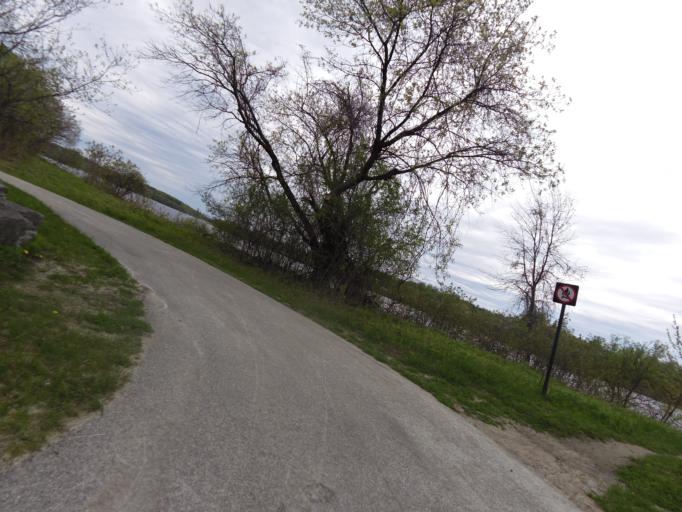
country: CA
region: Quebec
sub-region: Outaouais
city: Gatineau
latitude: 45.4733
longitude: -75.7331
